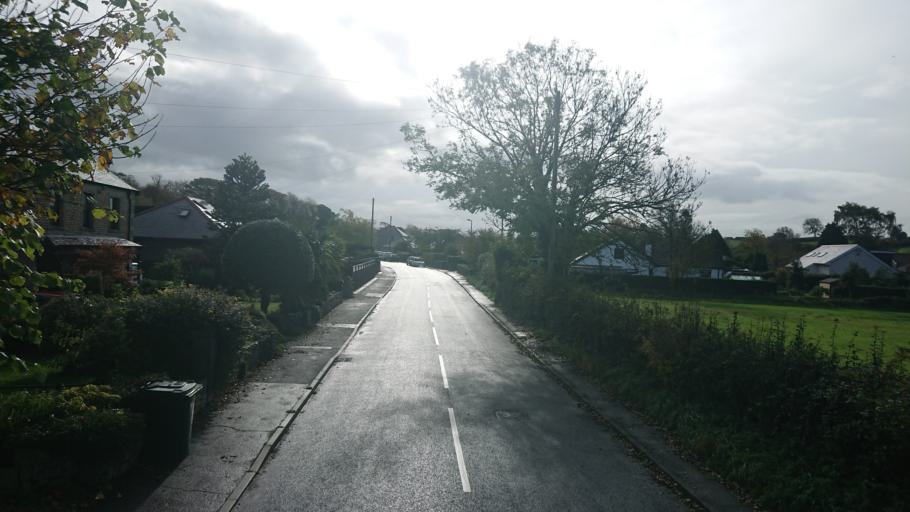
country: GB
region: England
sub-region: Lancashire
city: Bolton le Sands
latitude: 54.0794
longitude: -2.8038
